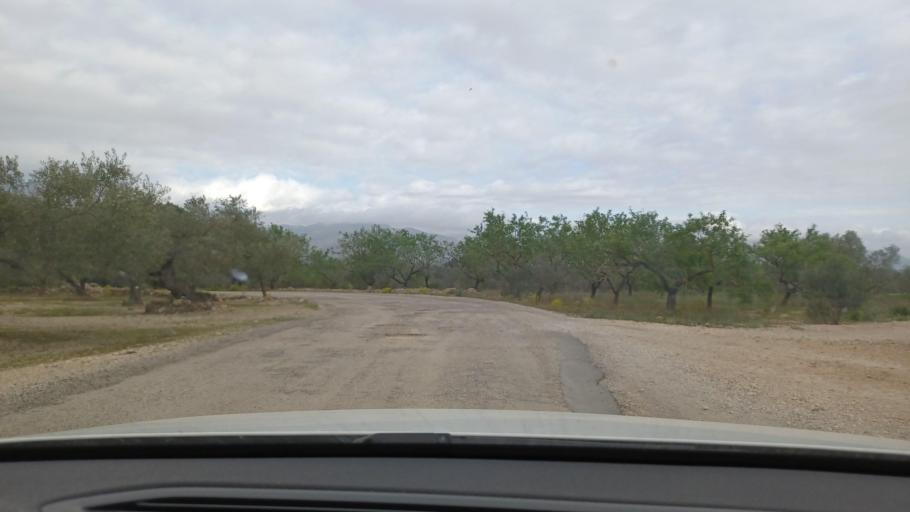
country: ES
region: Catalonia
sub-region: Provincia de Tarragona
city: Tortosa
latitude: 40.7912
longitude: 0.4759
